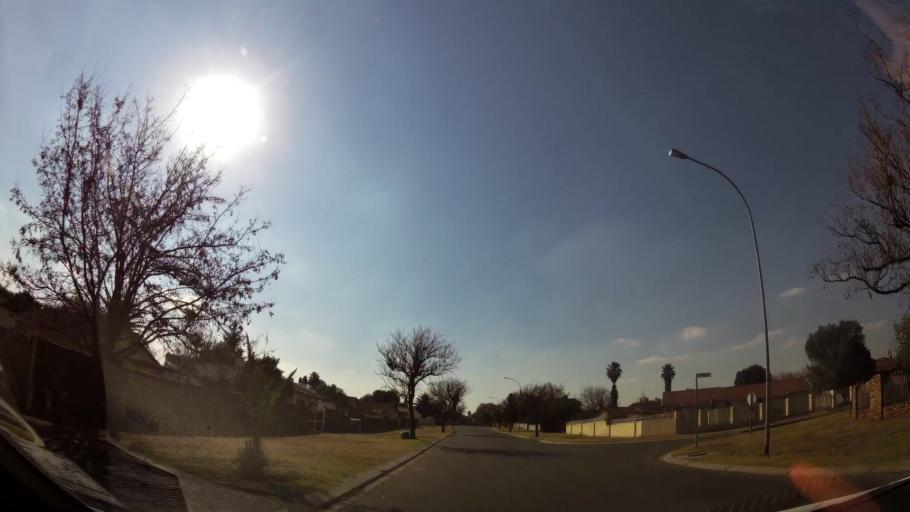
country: ZA
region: Gauteng
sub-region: Ekurhuleni Metropolitan Municipality
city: Brakpan
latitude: -26.2443
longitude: 28.3137
